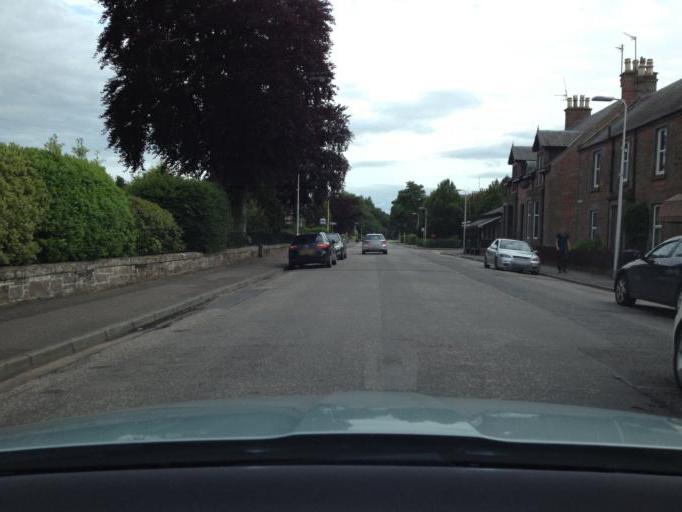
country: GB
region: Scotland
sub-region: Angus
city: Brechin
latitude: 56.8086
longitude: -2.6550
